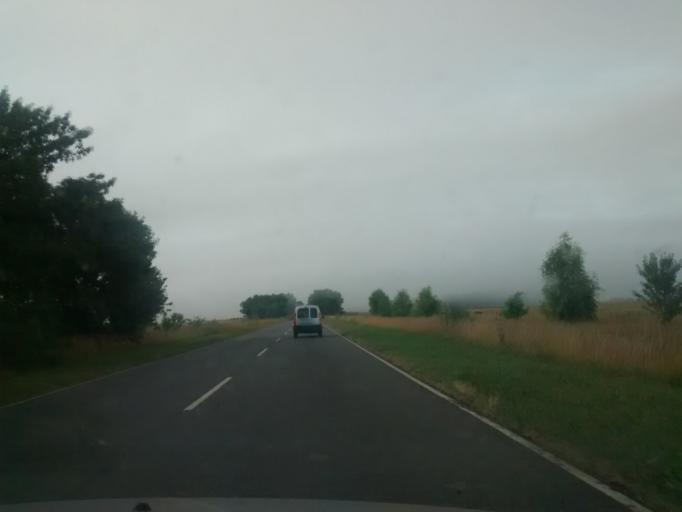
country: AR
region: Buenos Aires
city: Ranchos
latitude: -35.3502
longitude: -58.2476
